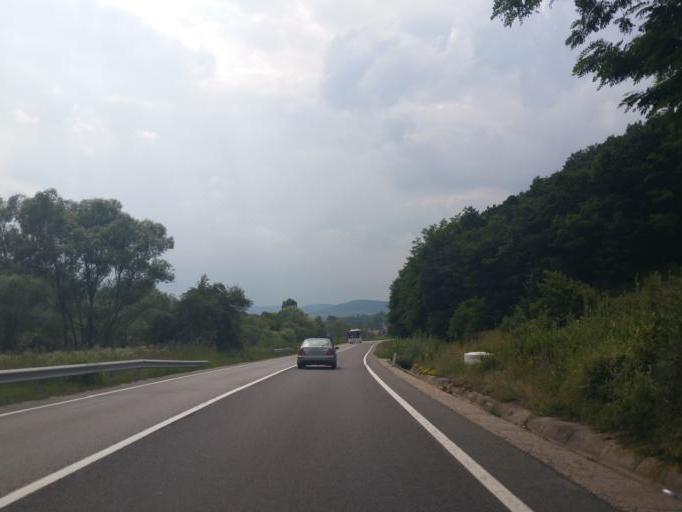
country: RO
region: Salaj
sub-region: Comuna Treznea
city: Treznea
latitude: 47.1231
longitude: 23.1468
